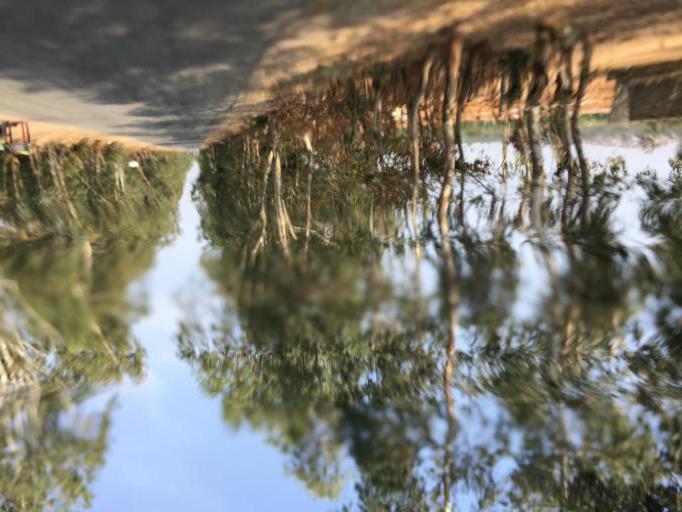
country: IN
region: Karnataka
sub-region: Chikkaballapur
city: Chik Ballapur
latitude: 13.3489
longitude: 77.6665
